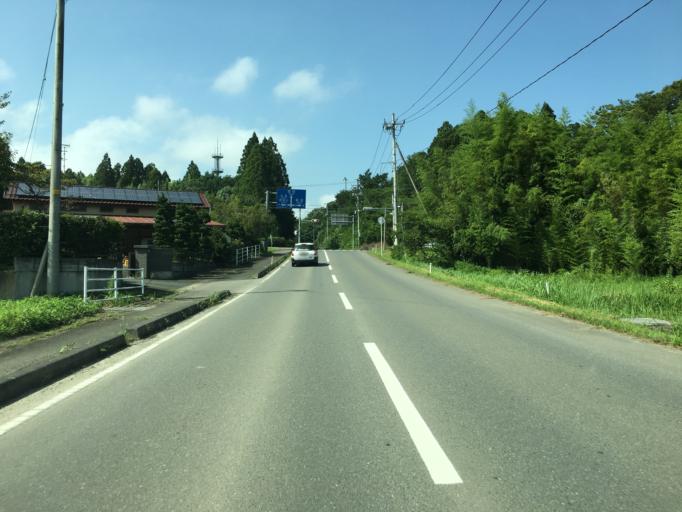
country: JP
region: Miyagi
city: Marumori
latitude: 37.8627
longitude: 140.8922
